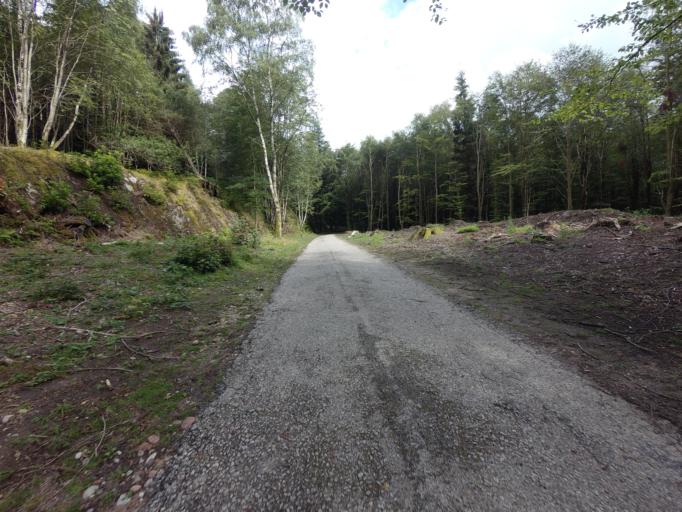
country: GB
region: Scotland
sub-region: Aberdeenshire
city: Banchory
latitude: 57.0605
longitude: -2.4486
